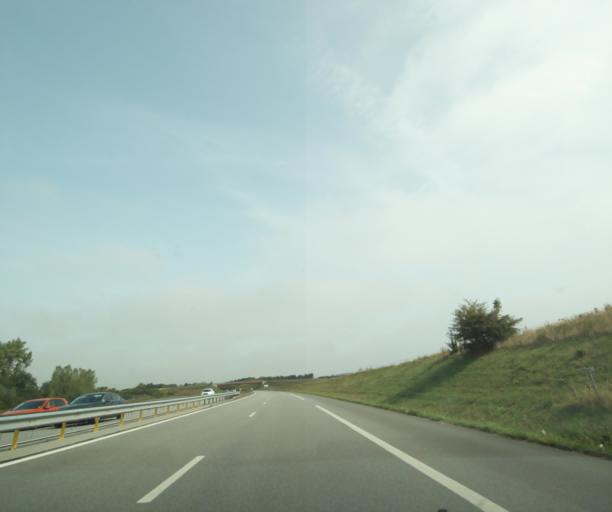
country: FR
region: Lower Normandy
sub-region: Departement de l'Orne
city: Sees
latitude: 48.6027
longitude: 0.1966
